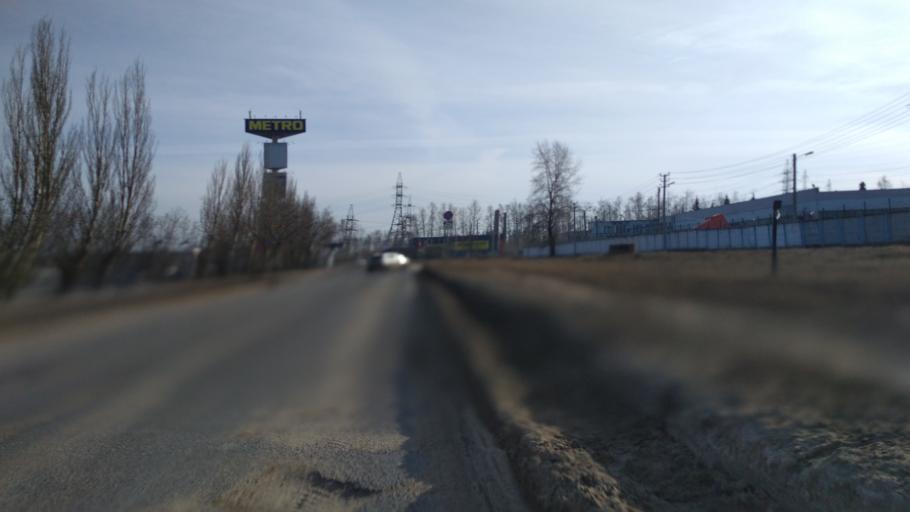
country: RU
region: Chuvashia
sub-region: Cheboksarskiy Rayon
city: Cheboksary
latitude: 56.1300
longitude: 47.3172
